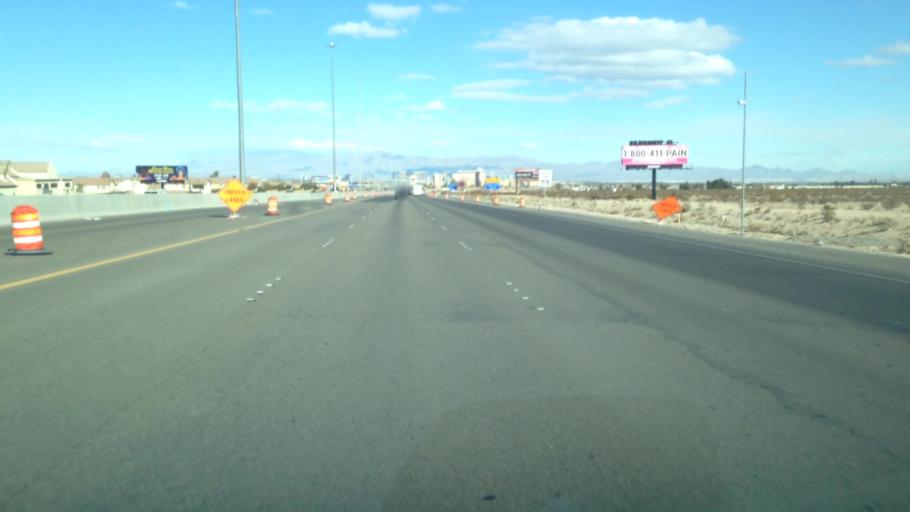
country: US
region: Nevada
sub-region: Clark County
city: Enterprise
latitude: 35.9714
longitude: -115.1814
